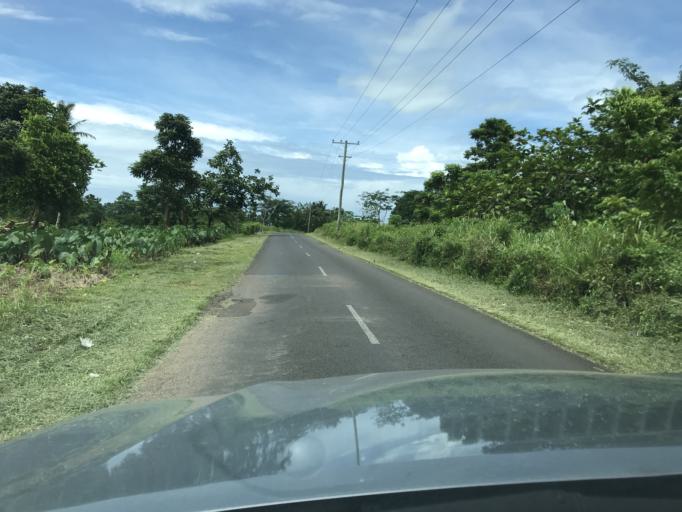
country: WS
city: Fasito`outa
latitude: -13.8630
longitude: -171.9106
